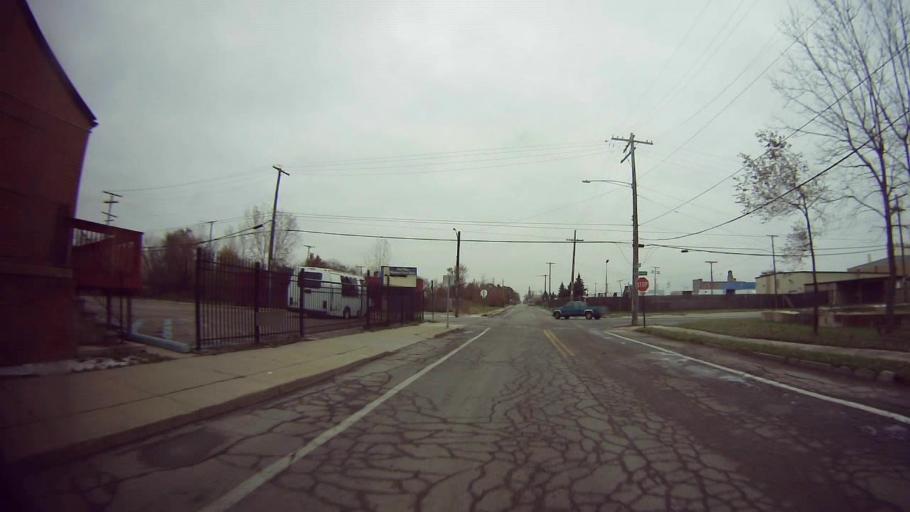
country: US
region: Michigan
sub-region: Wayne County
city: Hamtramck
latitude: 42.3689
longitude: -83.0472
